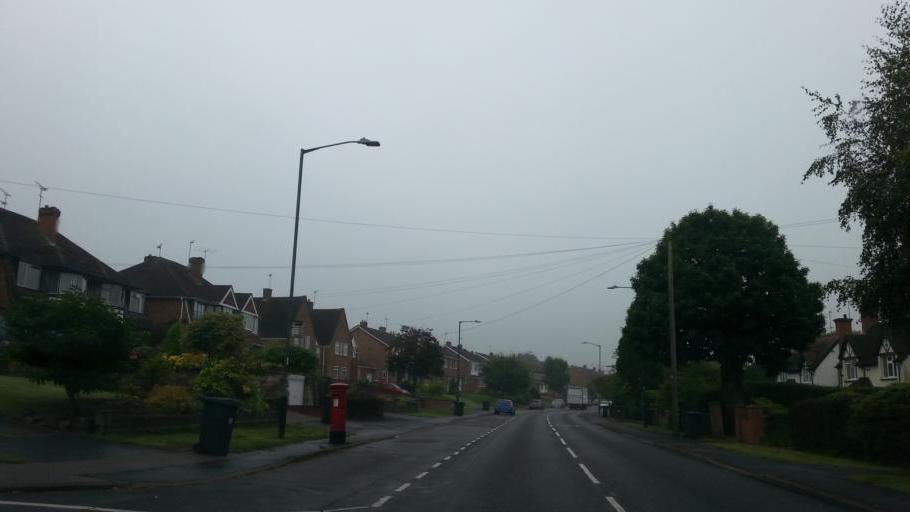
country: GB
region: England
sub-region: Warwickshire
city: Kenilworth
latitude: 52.3544
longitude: -1.5928
